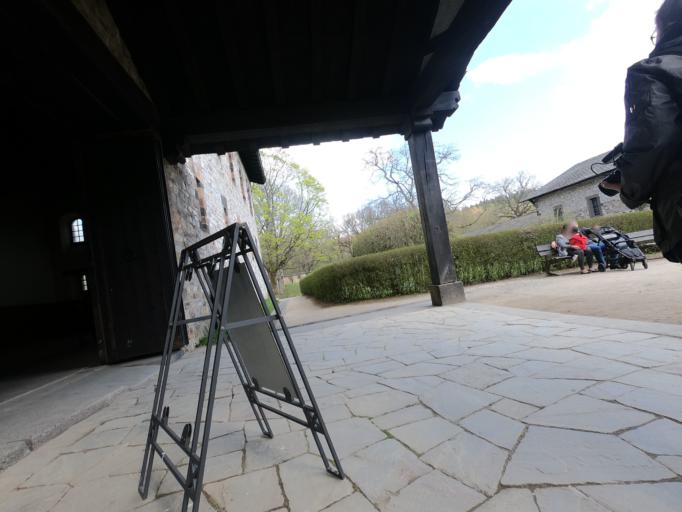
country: DE
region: Hesse
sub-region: Regierungsbezirk Darmstadt
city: Wehrheim
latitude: 50.2711
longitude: 8.5668
